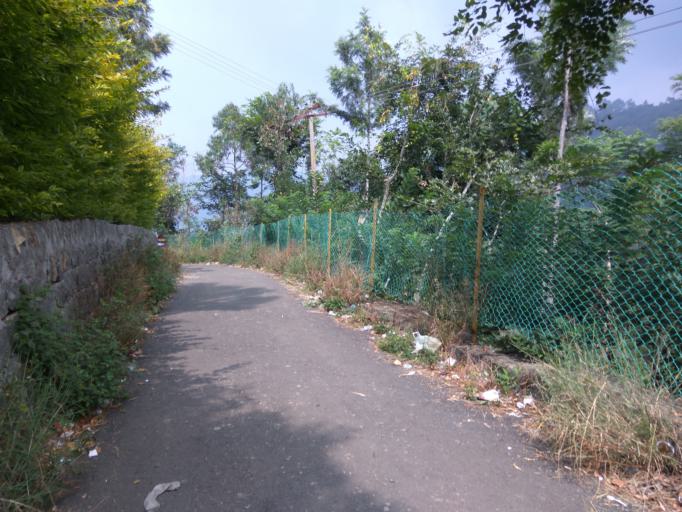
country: IN
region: Tamil Nadu
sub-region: Salem
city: Salem
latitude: 11.7947
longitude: 78.2010
